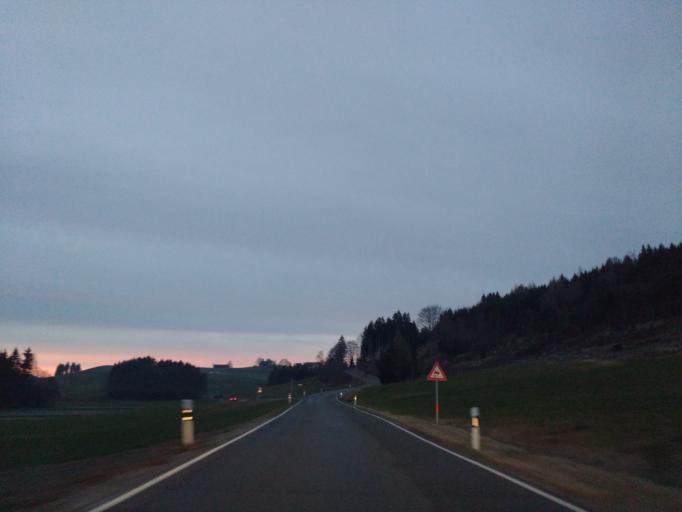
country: DE
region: Bavaria
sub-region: Upper Bavaria
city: Bernbeuren
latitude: 47.7597
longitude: 10.7558
